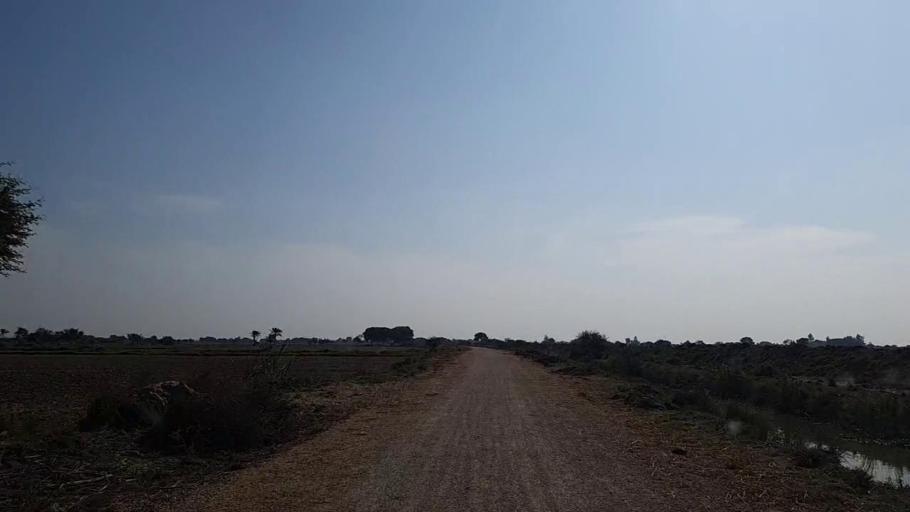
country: PK
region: Sindh
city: Daro Mehar
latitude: 24.7277
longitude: 68.1157
